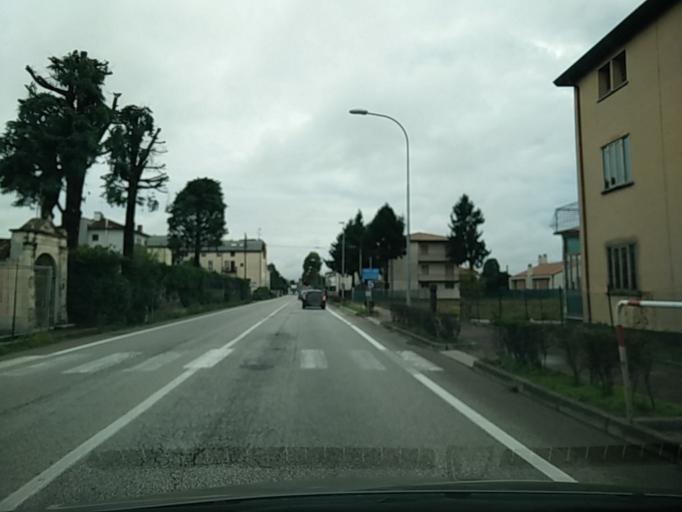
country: IT
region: Veneto
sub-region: Provincia di Padova
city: Cittadella
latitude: 45.6615
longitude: 11.7803
